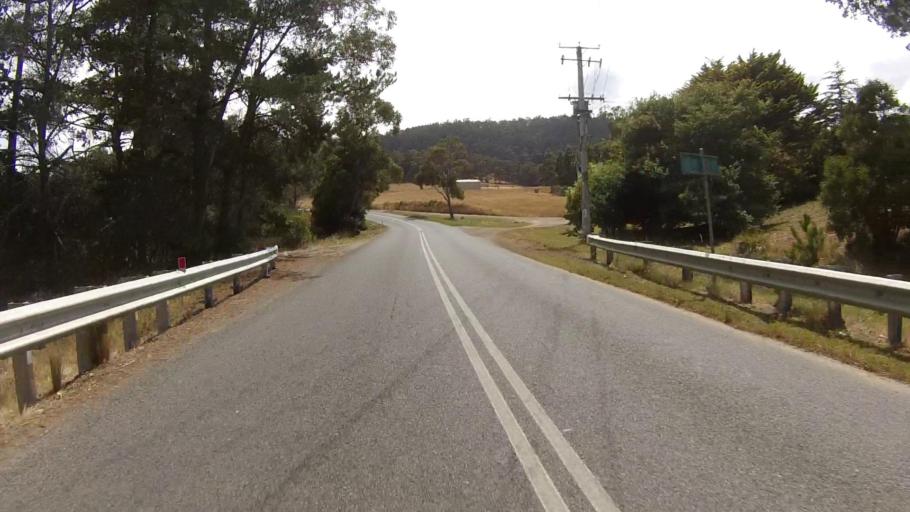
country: AU
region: Tasmania
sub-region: Huon Valley
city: Cygnet
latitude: -43.2109
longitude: 147.1158
